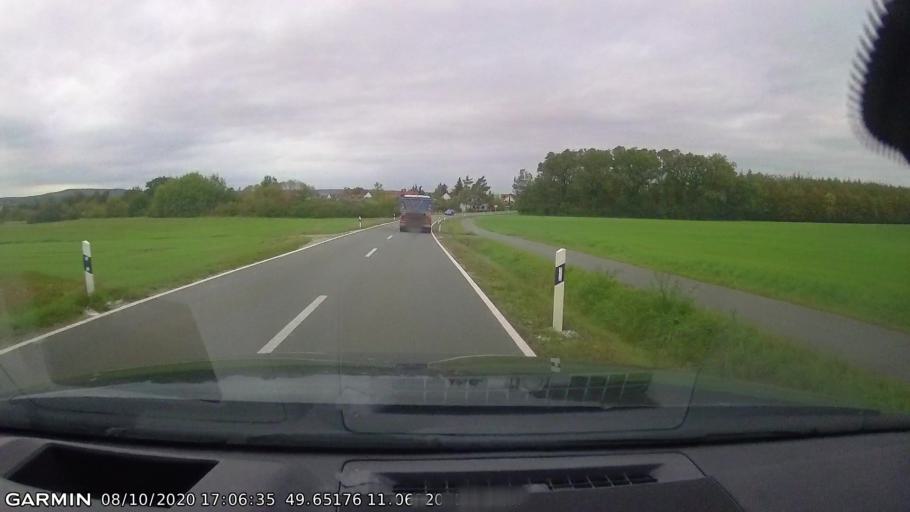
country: DE
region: Bavaria
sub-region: Upper Franconia
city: Langensendelbach
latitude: 49.6517
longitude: 11.0618
